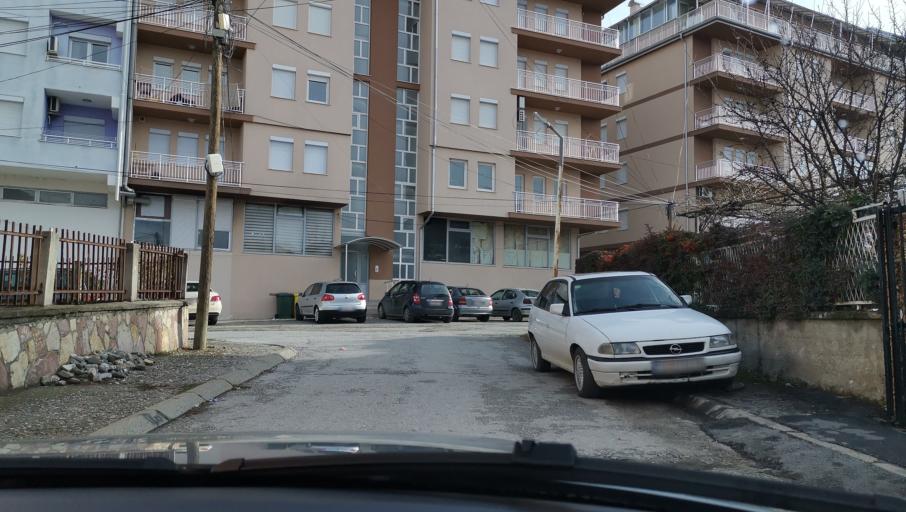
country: MK
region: Debar
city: Debar
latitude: 41.5179
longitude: 20.5294
